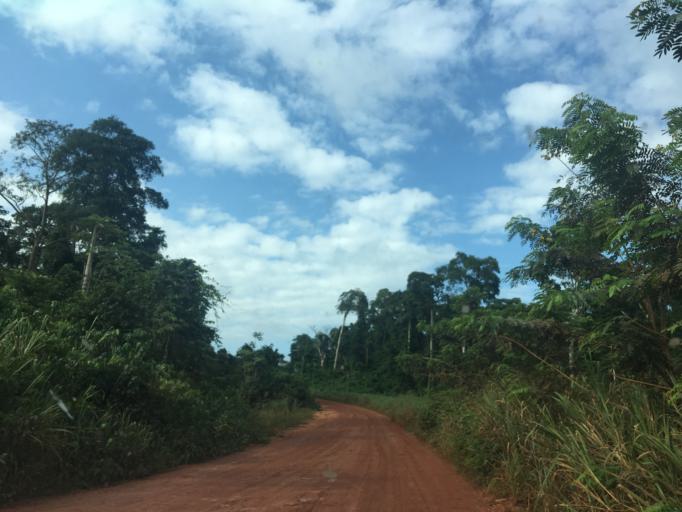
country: GH
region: Western
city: Wassa-Akropong
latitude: 5.9618
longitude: -2.4254
